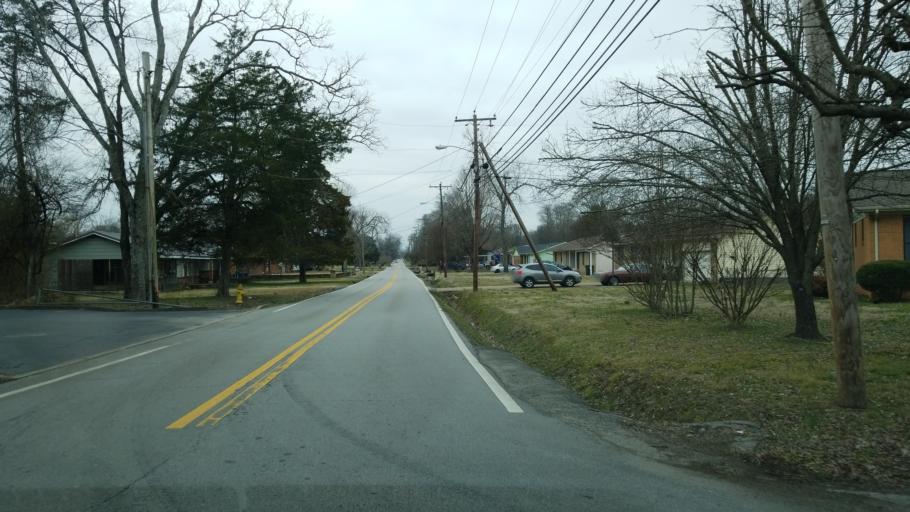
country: US
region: Tennessee
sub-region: Hamilton County
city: East Brainerd
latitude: 35.0531
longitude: -85.1522
